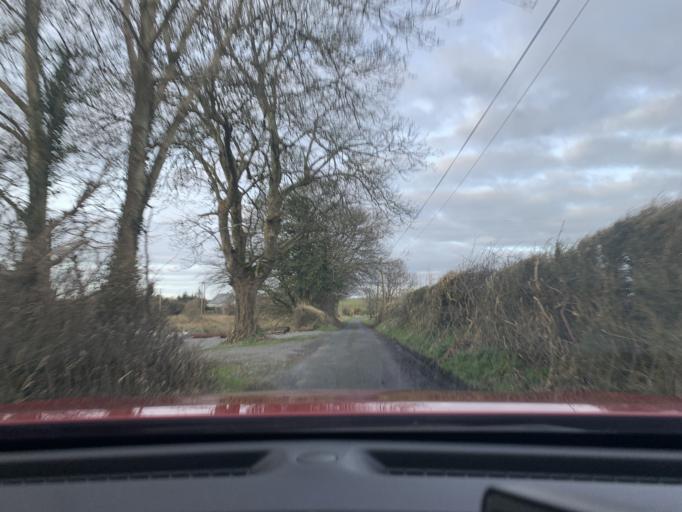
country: IE
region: Connaught
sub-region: Sligo
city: Ballymote
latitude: 54.0194
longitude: -8.5655
